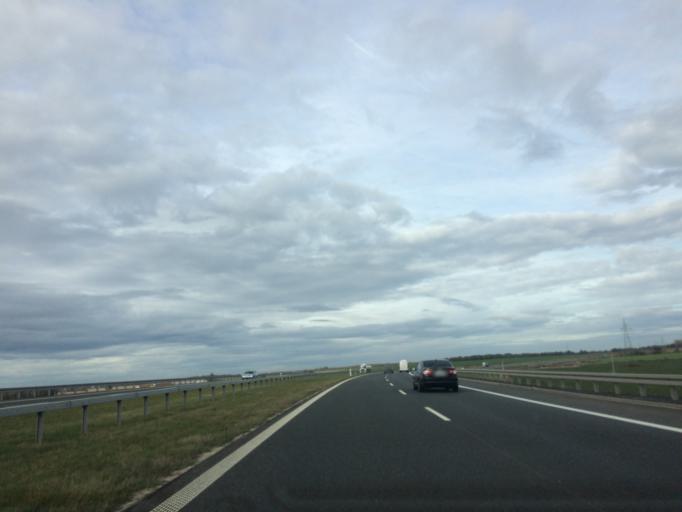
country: PL
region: Lower Silesian Voivodeship
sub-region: Powiat legnicki
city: Milkowice
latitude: 51.1825
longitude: 16.0870
